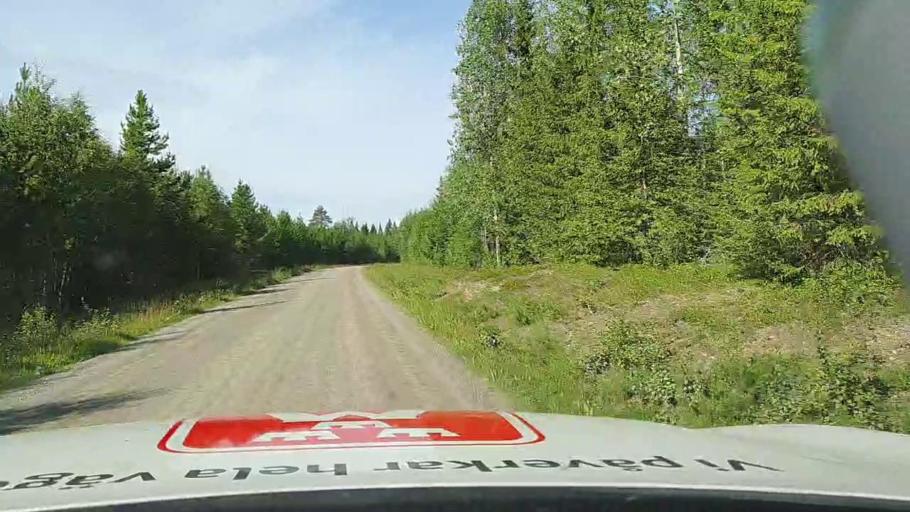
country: SE
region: Jaemtland
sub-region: Stroemsunds Kommun
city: Stroemsund
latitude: 63.7242
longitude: 15.2635
